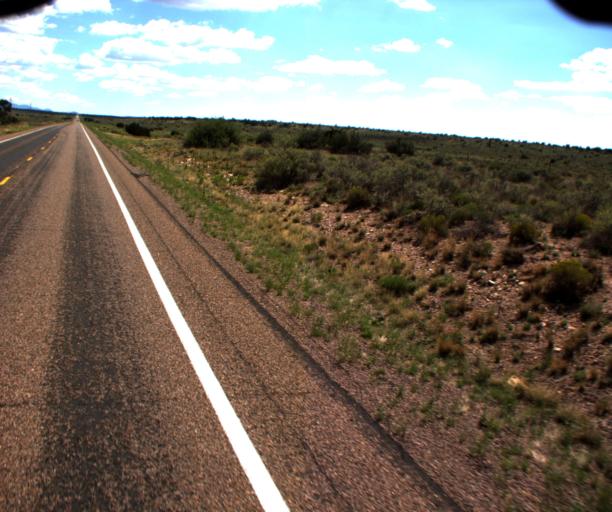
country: US
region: Arizona
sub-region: Coconino County
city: Williams
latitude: 35.5832
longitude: -112.1518
